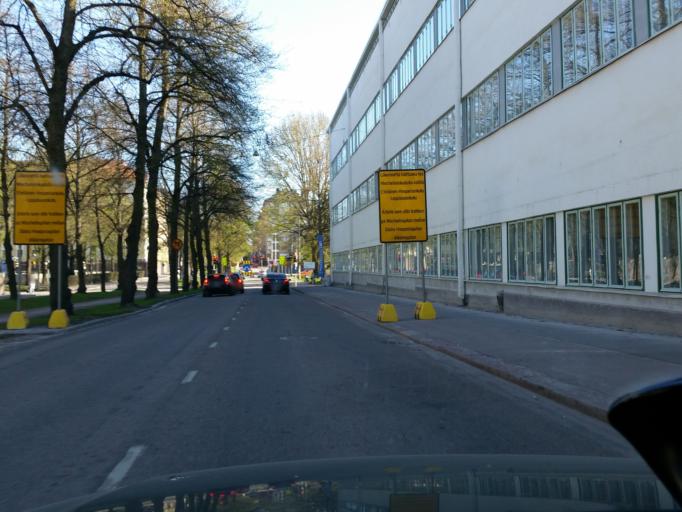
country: FI
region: Uusimaa
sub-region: Helsinki
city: Helsinki
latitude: 60.1775
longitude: 24.9171
